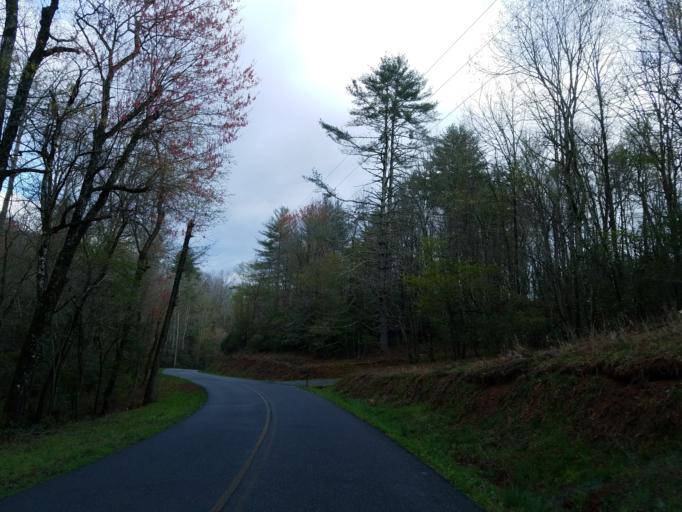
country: US
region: Georgia
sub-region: Fannin County
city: Blue Ridge
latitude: 34.7648
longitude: -84.2297
